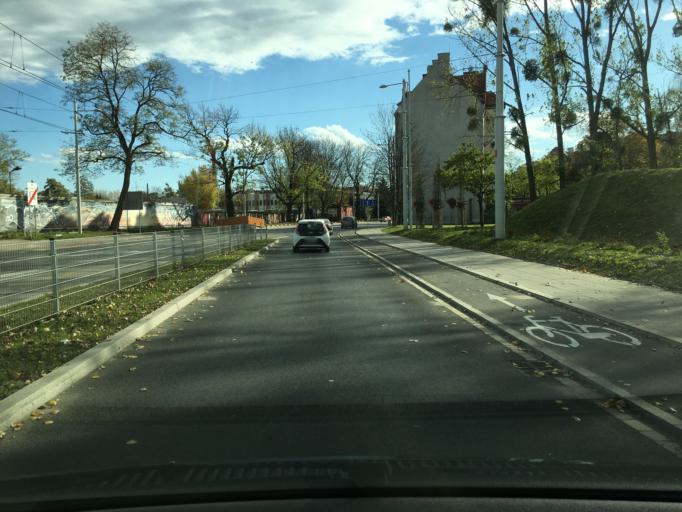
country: PL
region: Lower Silesian Voivodeship
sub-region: Powiat wroclawski
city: Wroclaw
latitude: 51.0957
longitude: 17.0419
